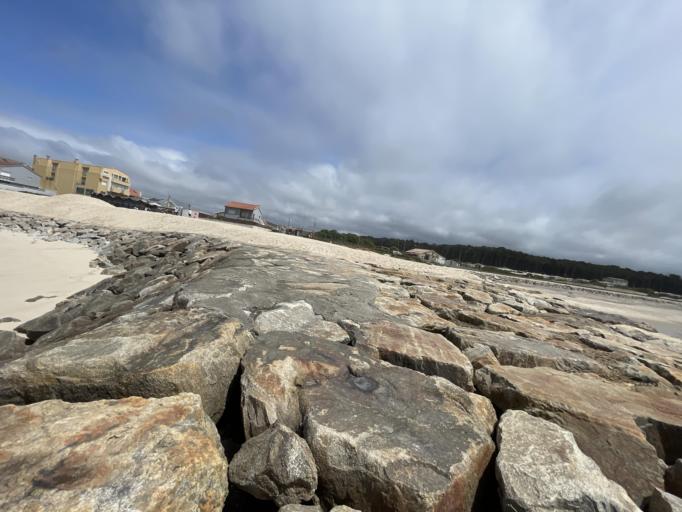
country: PT
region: Aveiro
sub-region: Ovar
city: Esmoriz
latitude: 40.9401
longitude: -8.6594
